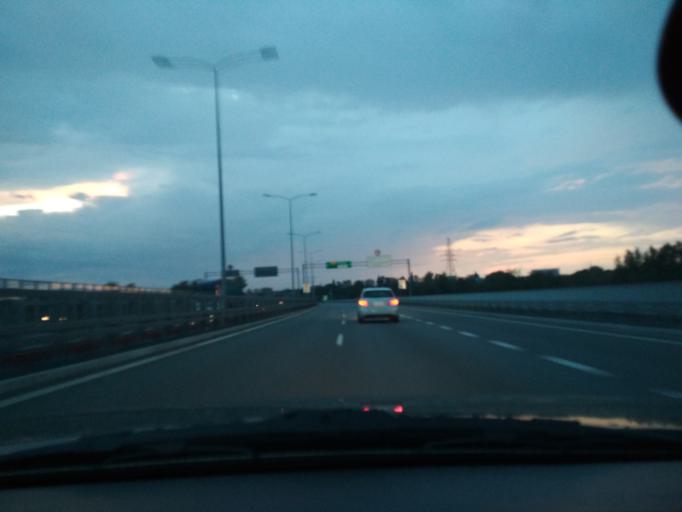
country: PL
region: Silesian Voivodeship
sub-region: Gliwice
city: Gliwice
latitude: 50.2856
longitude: 18.7088
